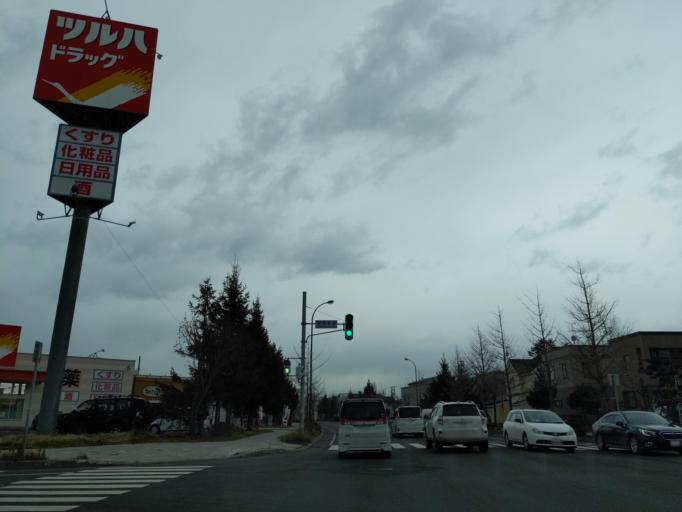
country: JP
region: Hokkaido
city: Sapporo
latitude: 43.1437
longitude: 141.3726
